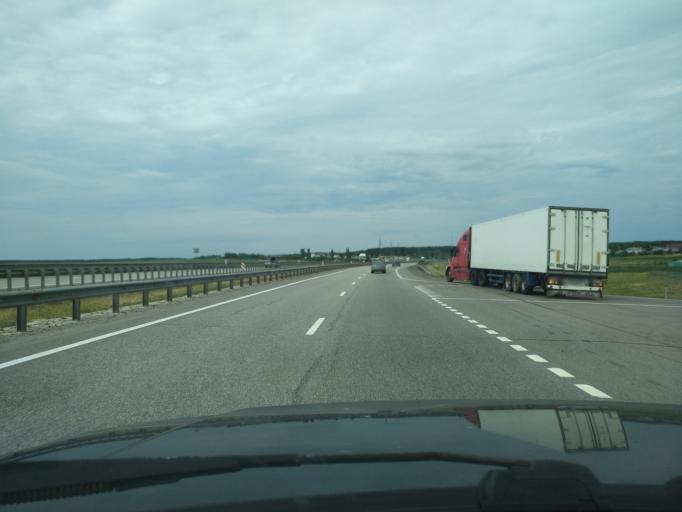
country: RU
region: Lipetsk
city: Khlevnoye
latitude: 52.0684
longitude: 39.1801
